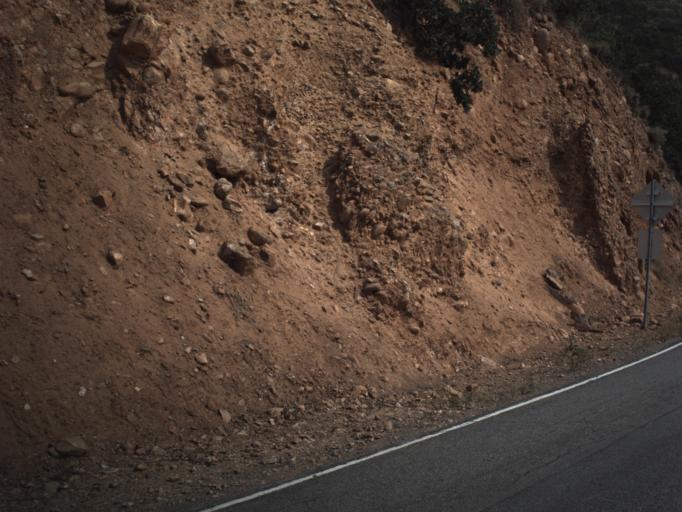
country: US
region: Utah
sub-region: Summit County
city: Summit Park
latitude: 40.8213
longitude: -111.6667
